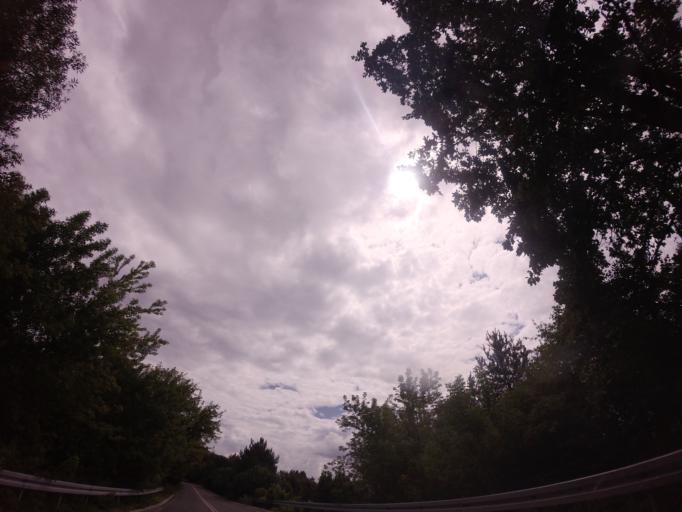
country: PL
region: Lublin Voivodeship
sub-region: Powiat pulawski
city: Kazimierz Dolny
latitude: 51.3056
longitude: 21.9511
